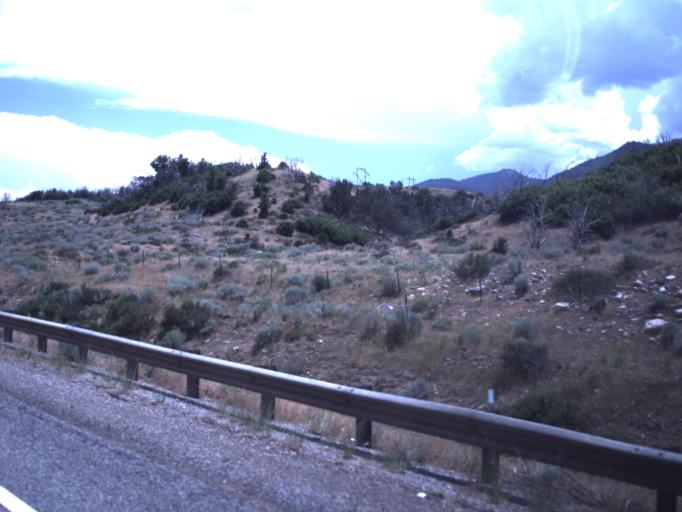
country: US
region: Utah
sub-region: Sanpete County
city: Fountain Green
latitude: 39.6988
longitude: -111.6973
